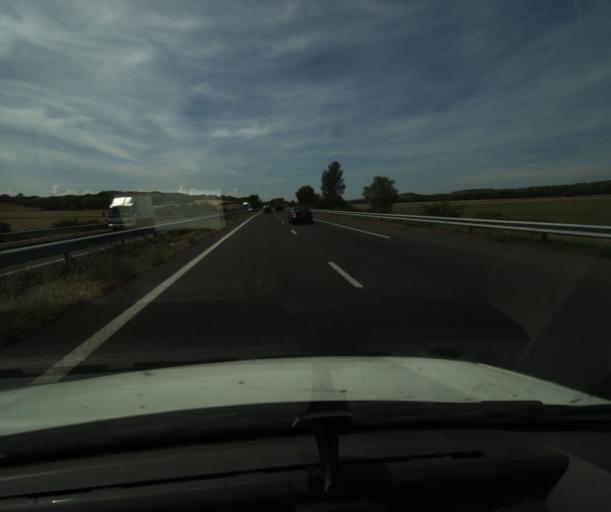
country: FR
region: Midi-Pyrenees
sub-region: Departement de la Haute-Garonne
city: Avignonet-Lauragais
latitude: 43.3259
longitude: 1.8549
